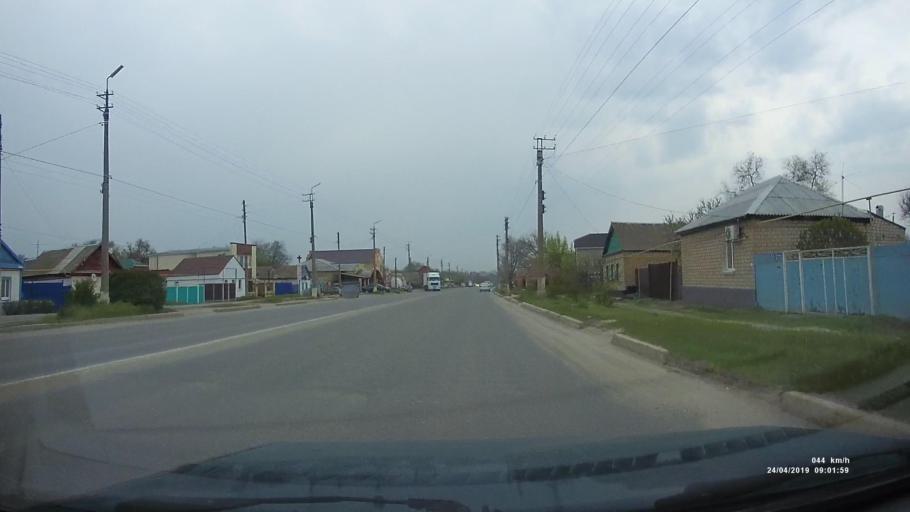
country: RU
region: Kalmykiya
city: Elista
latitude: 46.3124
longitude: 44.2296
